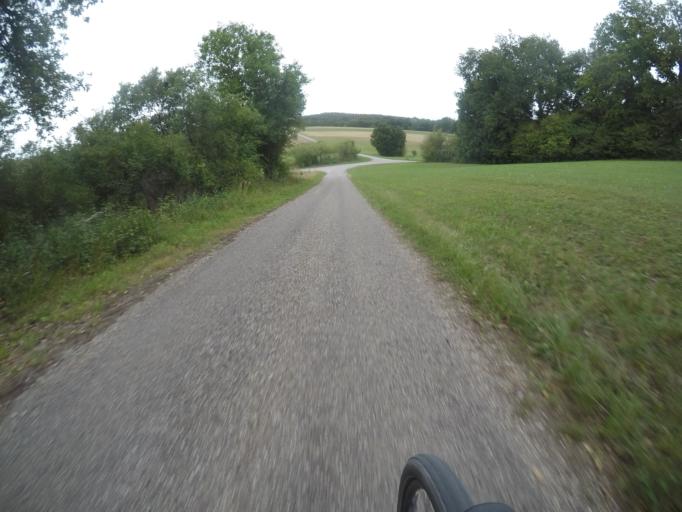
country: DE
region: Baden-Wuerttemberg
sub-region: Karlsruhe Region
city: Wurmberg
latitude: 48.8641
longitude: 8.8297
